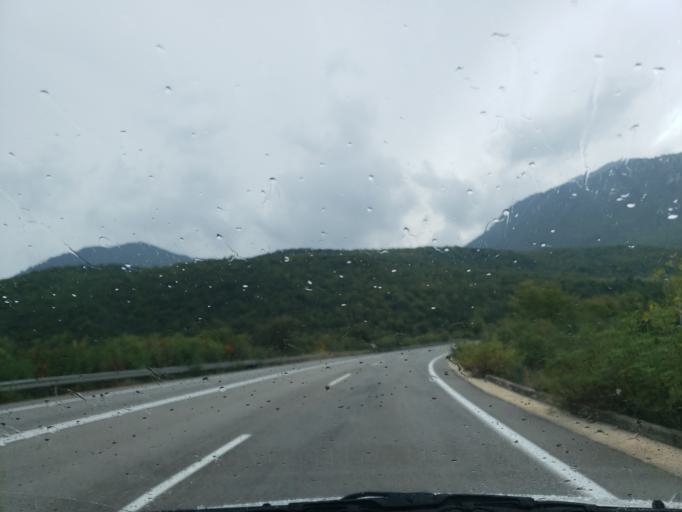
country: GR
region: Central Greece
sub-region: Nomos Fthiotidos
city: Anthili
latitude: 38.7906
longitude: 22.4934
